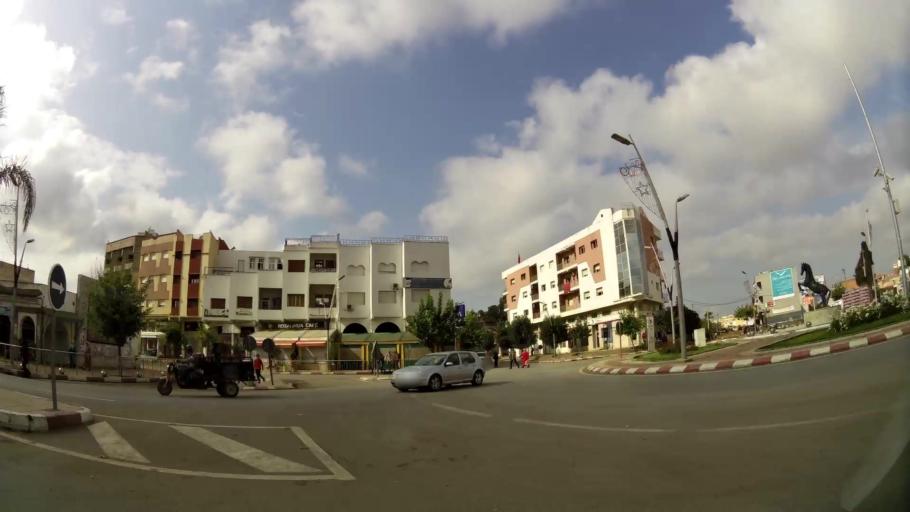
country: MA
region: Rabat-Sale-Zemmour-Zaer
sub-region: Khemisset
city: Tiflet
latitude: 33.8932
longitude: -6.3125
